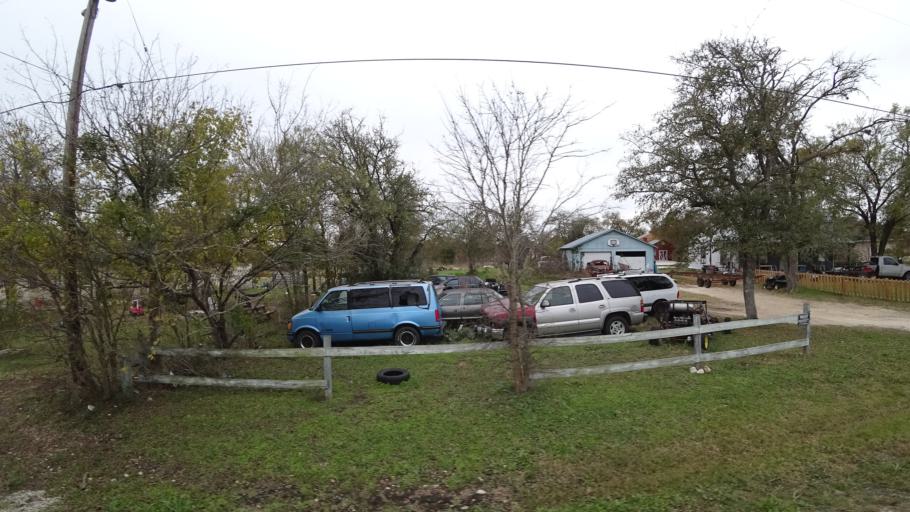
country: US
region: Texas
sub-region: Travis County
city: Garfield
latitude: 30.1041
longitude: -97.5737
